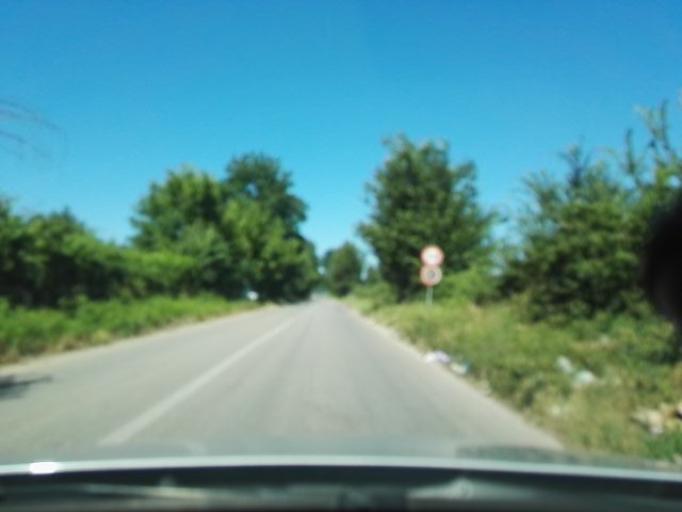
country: IT
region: Campania
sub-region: Provincia di Caserta
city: Casapesenna
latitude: 40.9855
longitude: 14.1479
